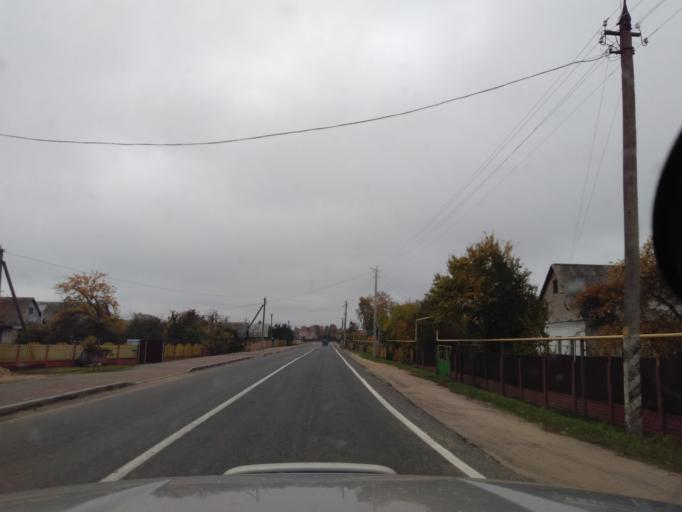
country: BY
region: Minsk
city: Kapyl'
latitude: 53.1430
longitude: 27.0914
